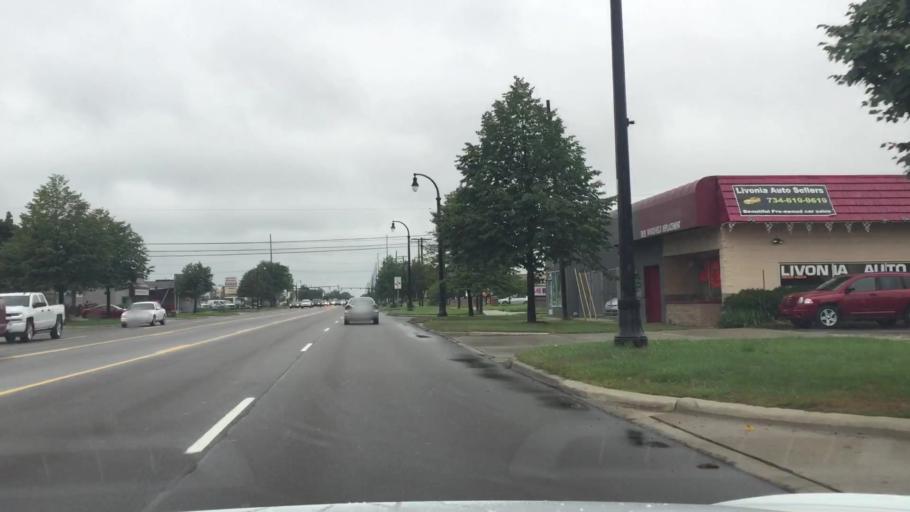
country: US
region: Michigan
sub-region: Wayne County
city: Livonia
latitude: 42.3694
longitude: -83.3291
